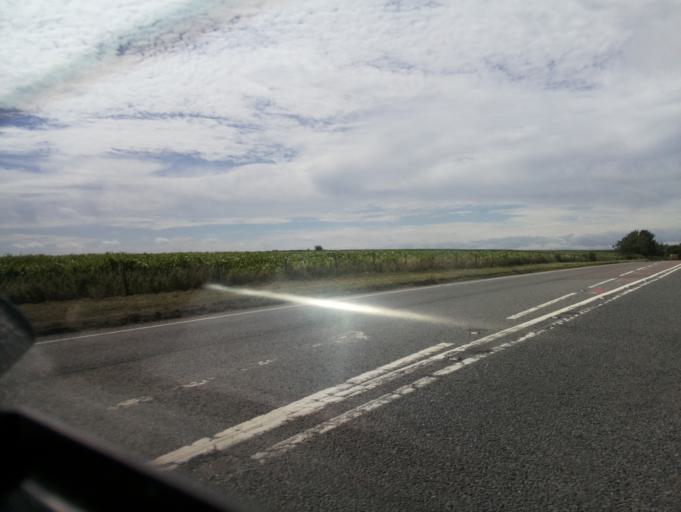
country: GB
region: England
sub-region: Dorset
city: Dorchester
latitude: 50.7692
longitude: -2.5356
